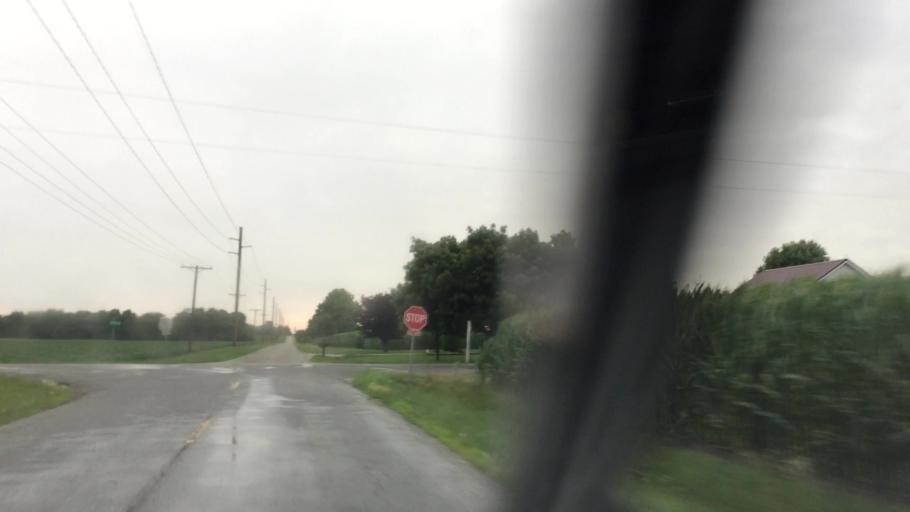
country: US
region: Iowa
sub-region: Lee County
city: Fort Madison
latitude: 40.5950
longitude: -91.2678
